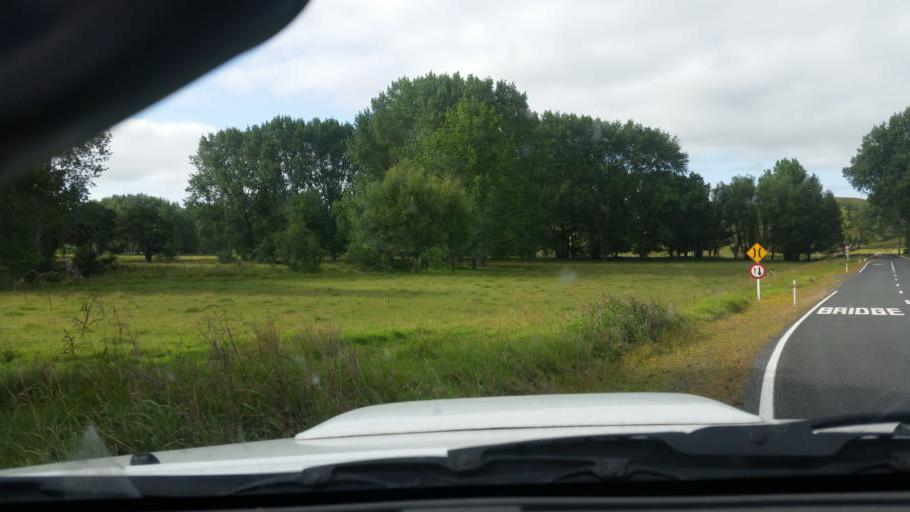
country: NZ
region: Northland
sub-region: Kaipara District
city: Dargaville
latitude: -35.8399
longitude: 173.8446
